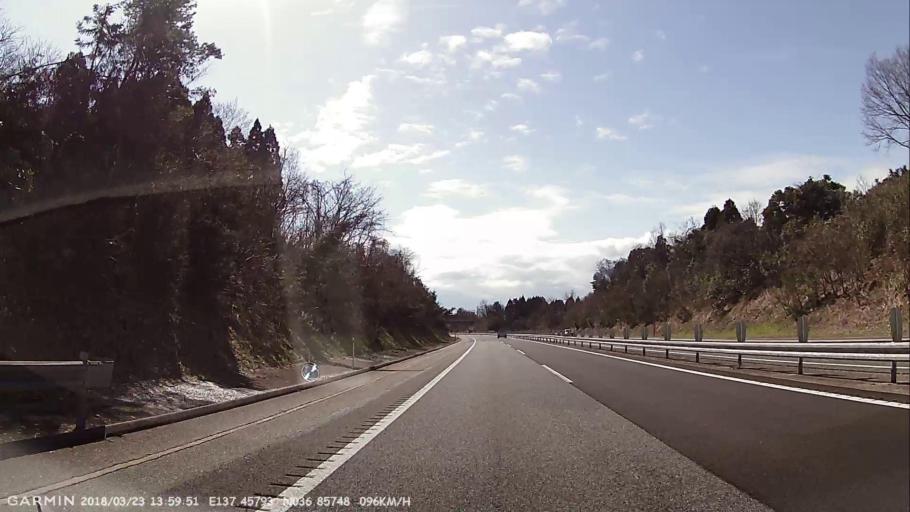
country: JP
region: Toyama
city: Uozu
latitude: 36.8574
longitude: 137.4575
